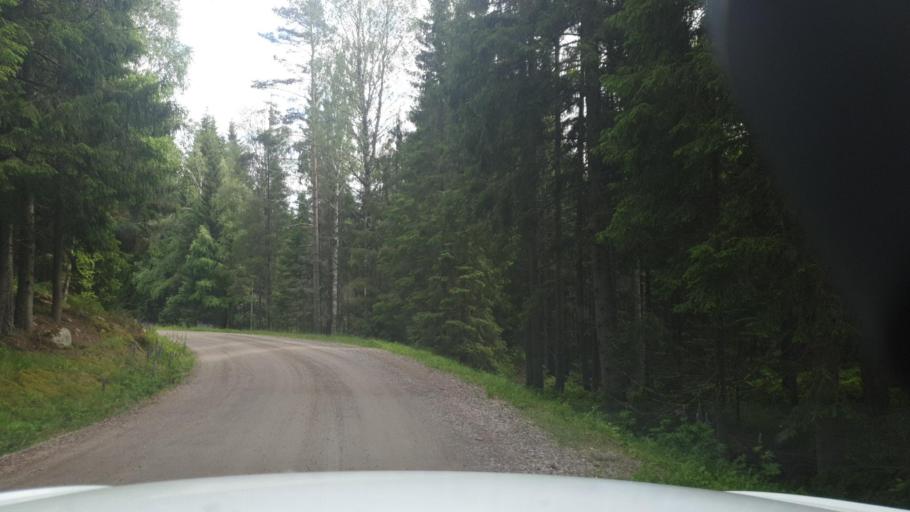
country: NO
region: Ostfold
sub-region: Romskog
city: Romskog
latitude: 59.7132
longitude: 12.0211
